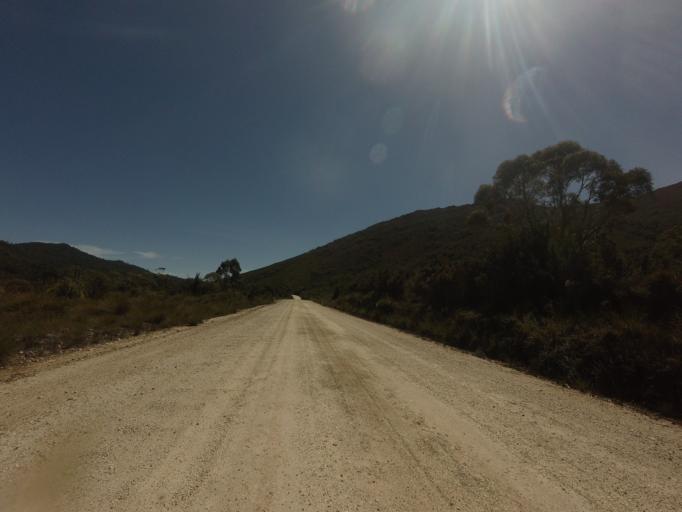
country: AU
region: Tasmania
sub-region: Huon Valley
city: Geeveston
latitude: -42.9373
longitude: 146.3477
